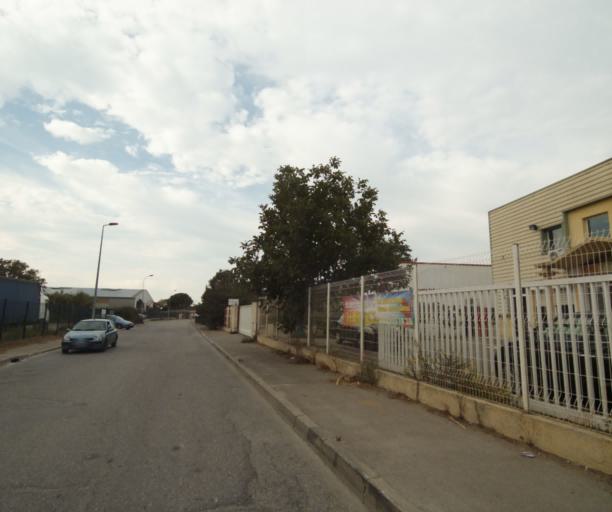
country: FR
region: Provence-Alpes-Cote d'Azur
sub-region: Departement des Bouches-du-Rhone
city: Marignane
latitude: 43.4066
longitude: 5.2026
